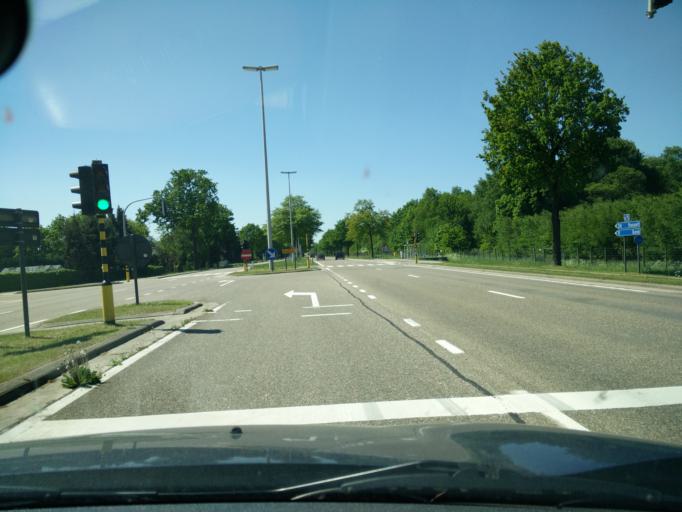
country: BE
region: Flanders
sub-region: Provincie Limburg
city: As
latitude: 51.0094
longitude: 5.6412
